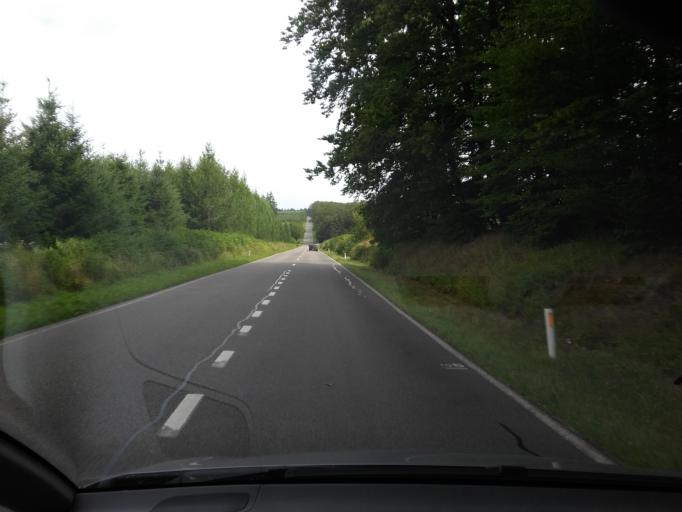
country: BE
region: Wallonia
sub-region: Province du Luxembourg
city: Chiny
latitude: 49.7581
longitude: 5.3170
